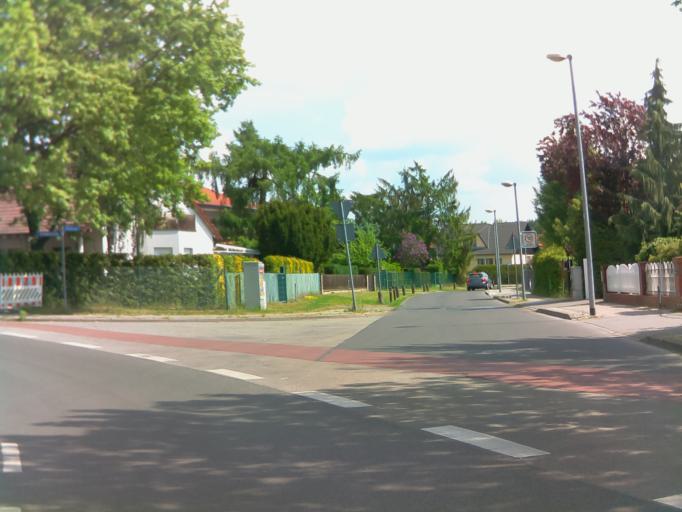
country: DE
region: Brandenburg
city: Dallgow-Doeberitz
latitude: 52.5466
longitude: 13.0667
